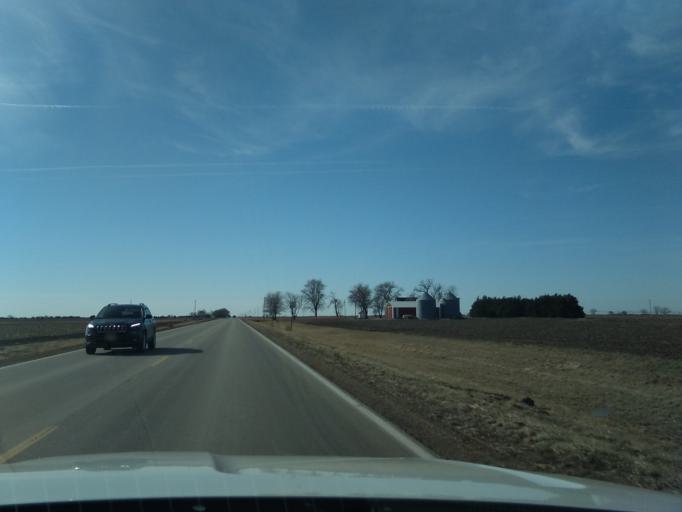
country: US
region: Nebraska
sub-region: Saline County
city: Friend
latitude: 40.8173
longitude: -97.2920
